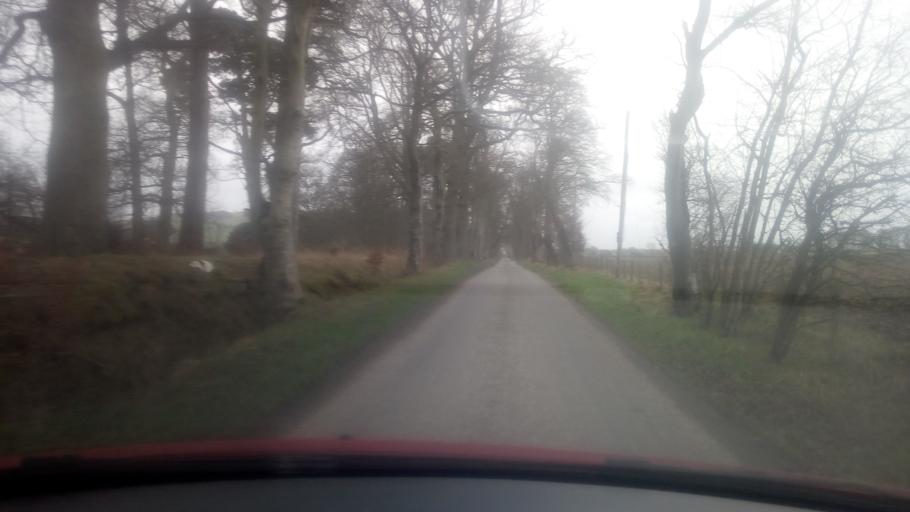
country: GB
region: Scotland
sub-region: The Scottish Borders
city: Jedburgh
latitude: 55.4256
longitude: -2.6415
